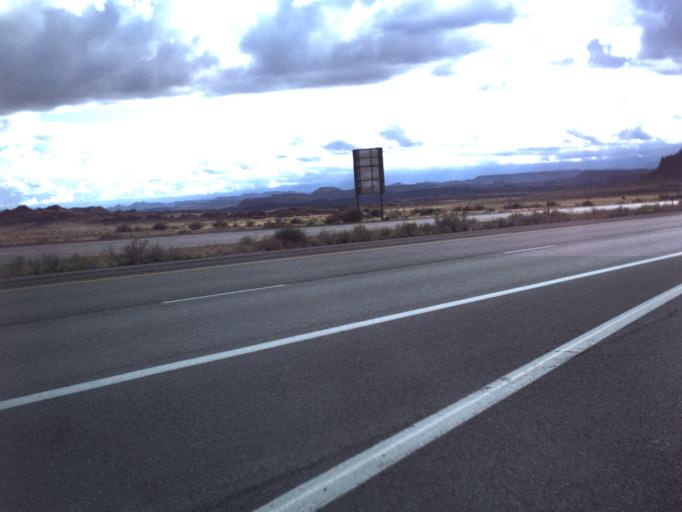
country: US
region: Utah
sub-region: Emery County
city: Ferron
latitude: 38.8406
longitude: -111.0685
